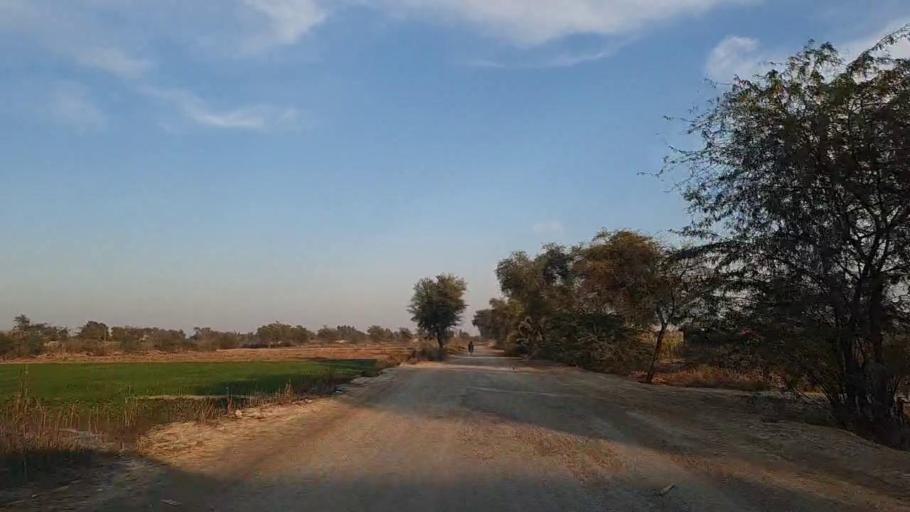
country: PK
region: Sindh
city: Bandhi
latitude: 26.5974
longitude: 68.3454
